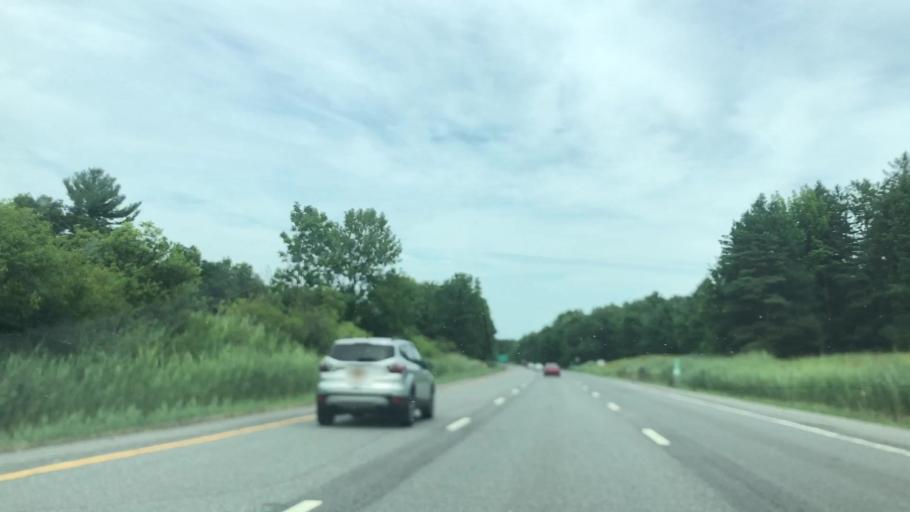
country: US
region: New York
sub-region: Saratoga County
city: Saratoga Springs
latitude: 43.0732
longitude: -73.7502
